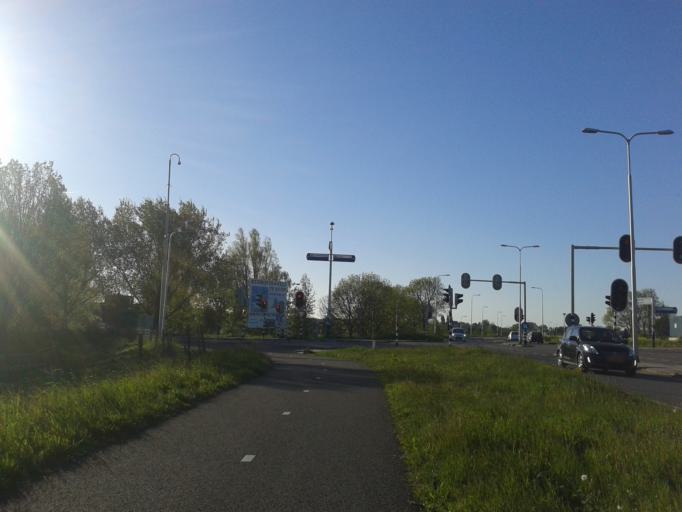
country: NL
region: South Holland
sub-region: Gemeente Waddinxveen
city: Waddinxveen
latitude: 52.0313
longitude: 4.6550
